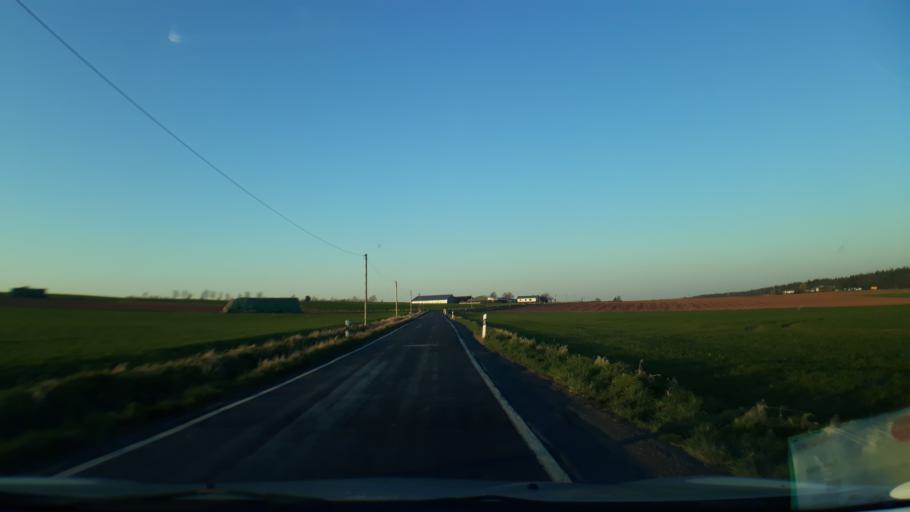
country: DE
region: North Rhine-Westphalia
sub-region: Regierungsbezirk Koln
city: Mechernich
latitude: 50.6122
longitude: 6.5974
